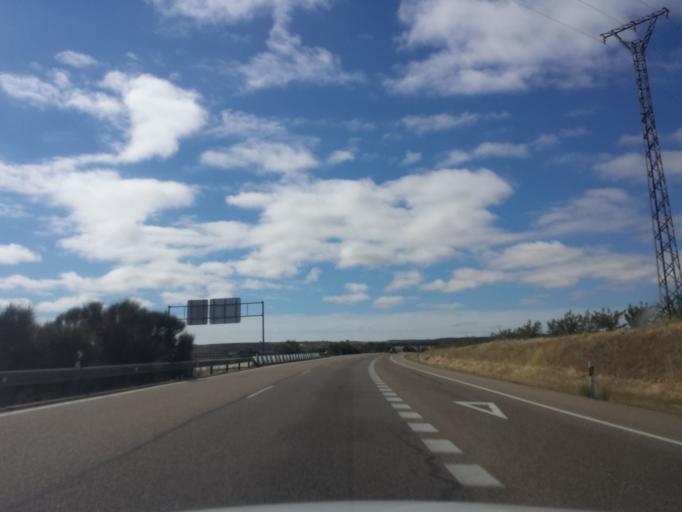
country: ES
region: Castille and Leon
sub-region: Provincia de Valladolid
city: Villardefrades
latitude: 41.7251
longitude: -5.2489
